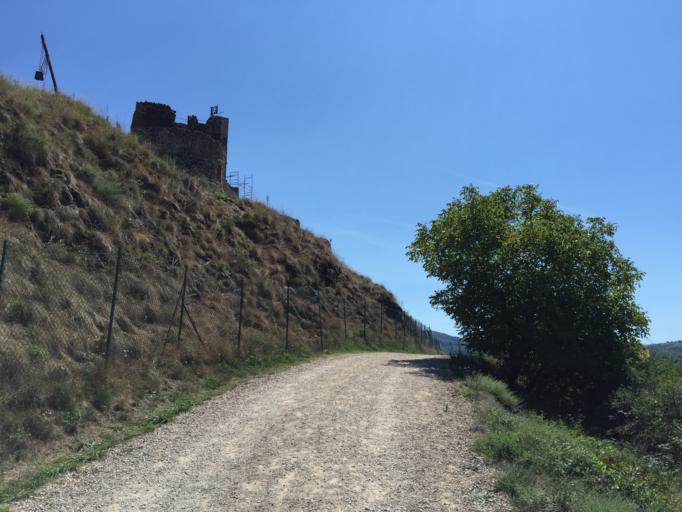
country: FR
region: Midi-Pyrenees
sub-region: Departement de l'Aveyron
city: Espalion
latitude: 44.5182
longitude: 2.7517
